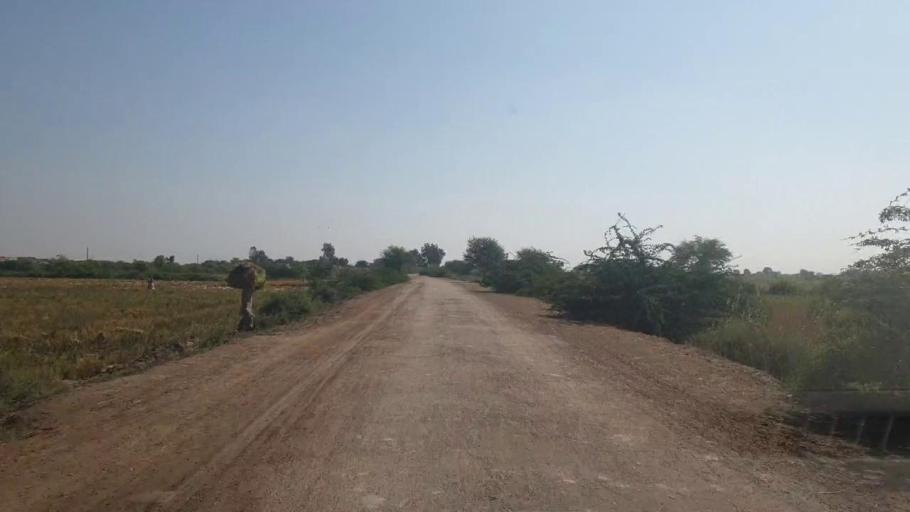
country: PK
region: Sindh
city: Badin
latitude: 24.5735
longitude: 68.8440
